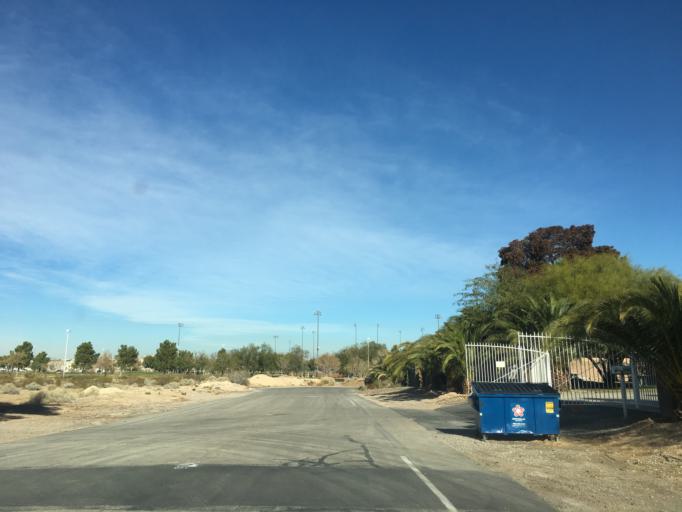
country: US
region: Nevada
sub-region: Clark County
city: Enterprise
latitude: 36.0091
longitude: -115.1657
